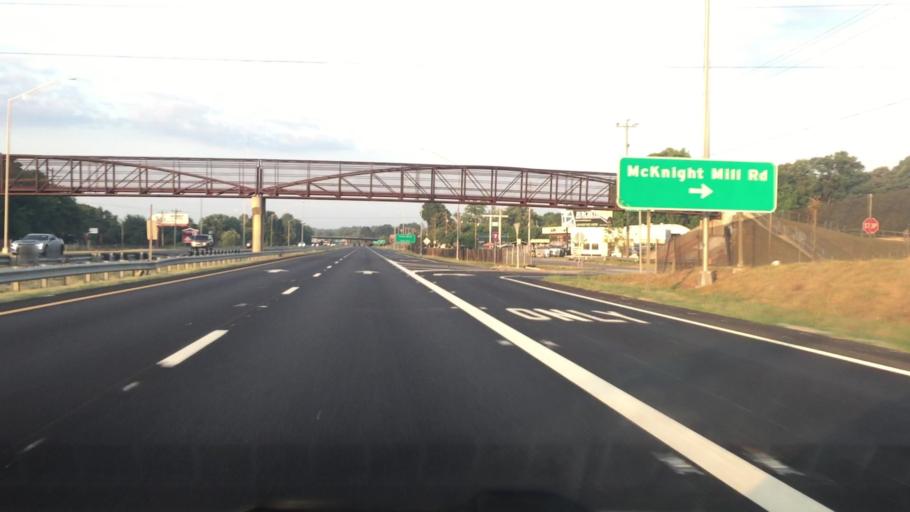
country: US
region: North Carolina
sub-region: Guilford County
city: Greensboro
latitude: 36.1188
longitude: -79.7530
